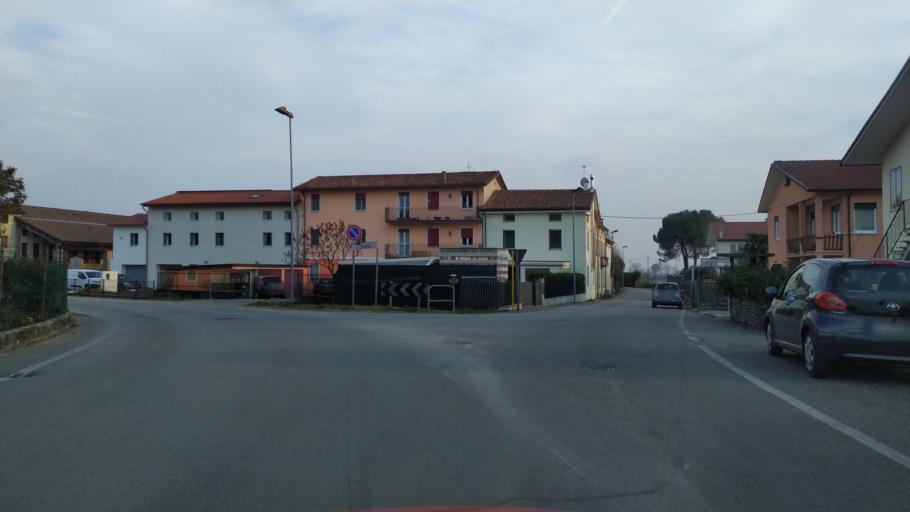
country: IT
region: Veneto
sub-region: Provincia di Vicenza
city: Marano Vicentino
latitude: 45.6903
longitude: 11.4356
